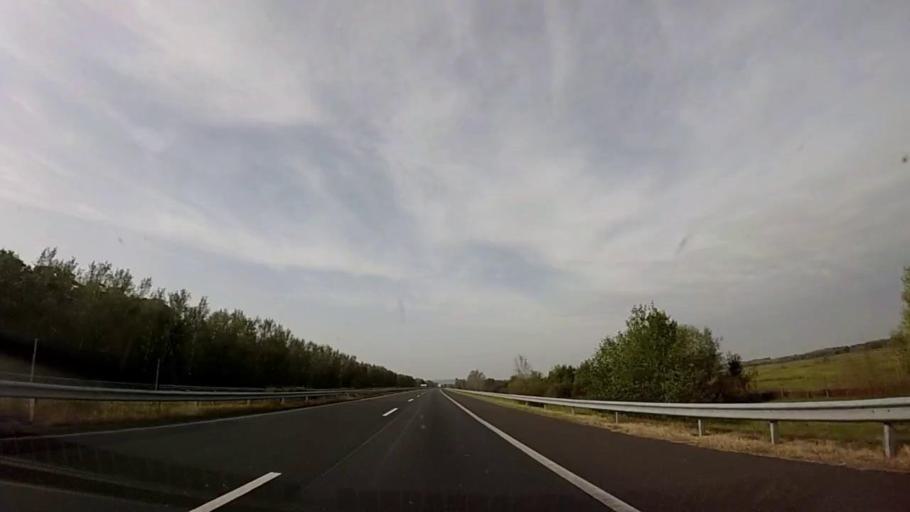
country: HU
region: Somogy
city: Kethely
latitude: 46.6894
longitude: 17.4278
